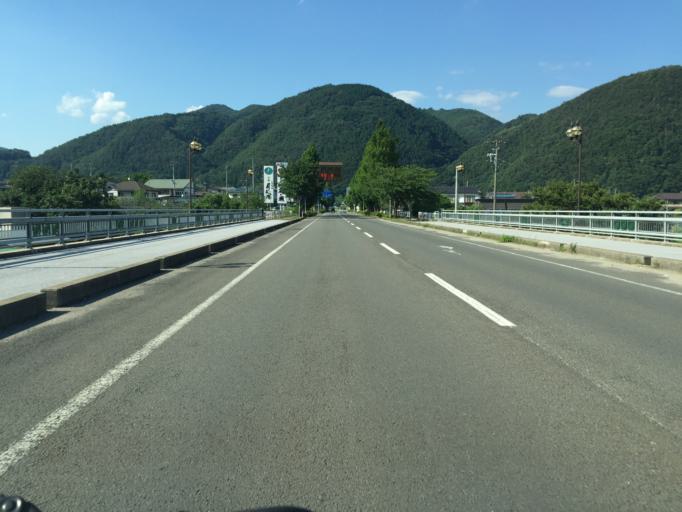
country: JP
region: Fukushima
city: Fukushima-shi
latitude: 37.8350
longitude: 140.4446
